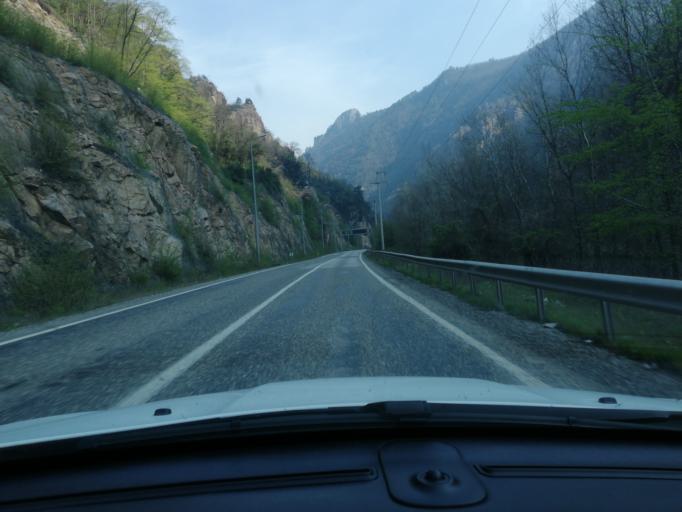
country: TR
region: Karabuk
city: Yenice
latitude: 41.1753
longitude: 32.4465
